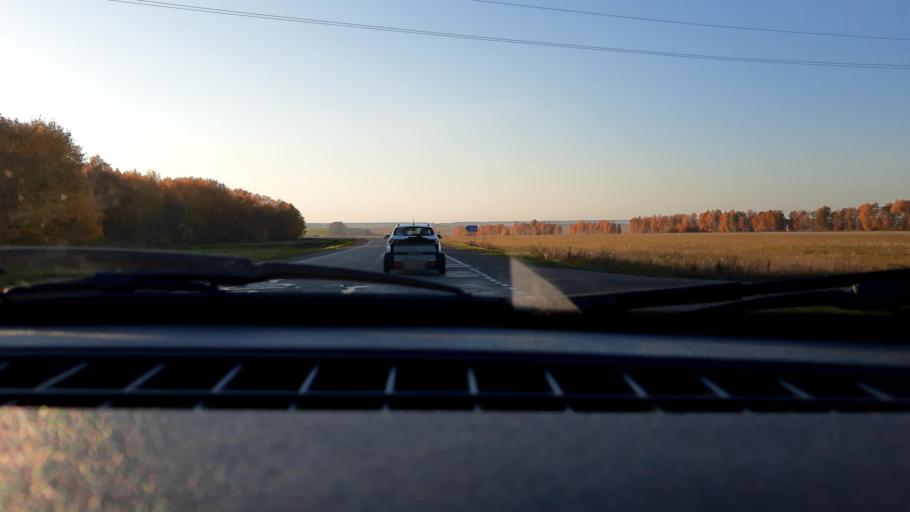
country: RU
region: Bashkortostan
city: Asanovo
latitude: 54.8260
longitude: 55.6423
